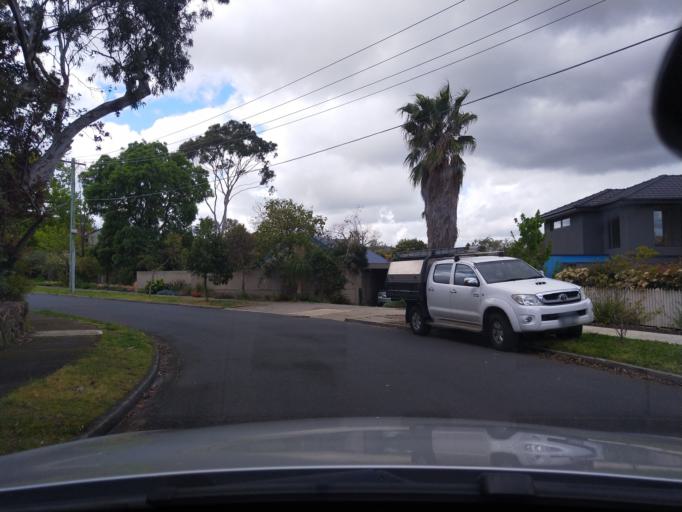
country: AU
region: Victoria
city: Macleod
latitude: -37.7406
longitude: 145.0719
